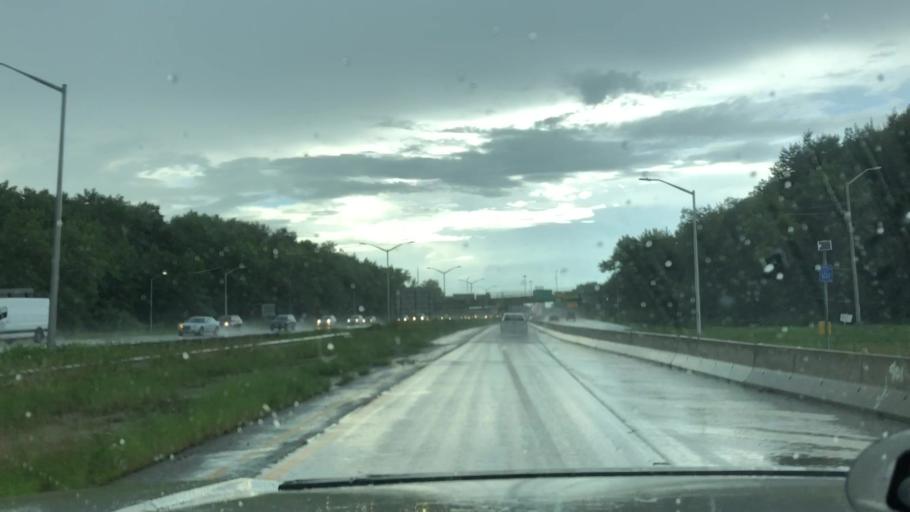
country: US
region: New Jersey
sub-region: Middlesex County
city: Sewaren
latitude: 40.5261
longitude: -74.2266
